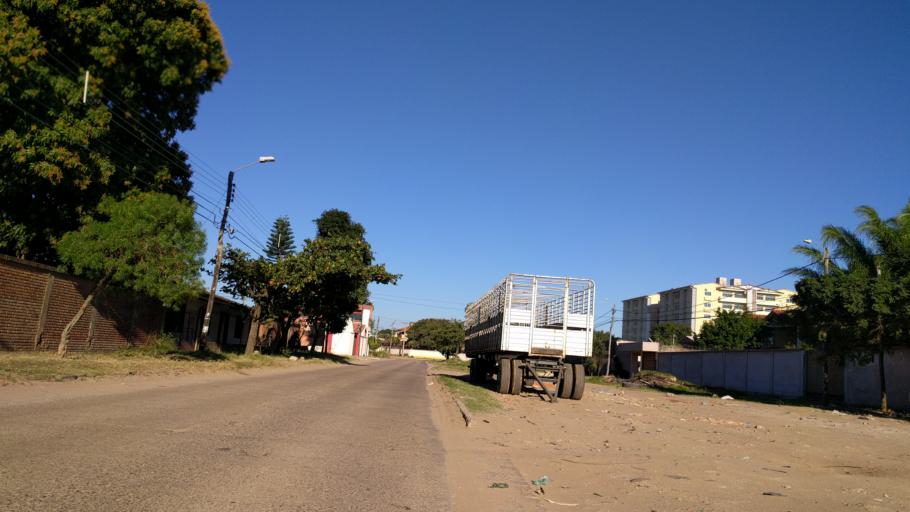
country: BO
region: Santa Cruz
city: Santa Cruz de la Sierra
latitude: -17.8034
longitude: -63.2194
